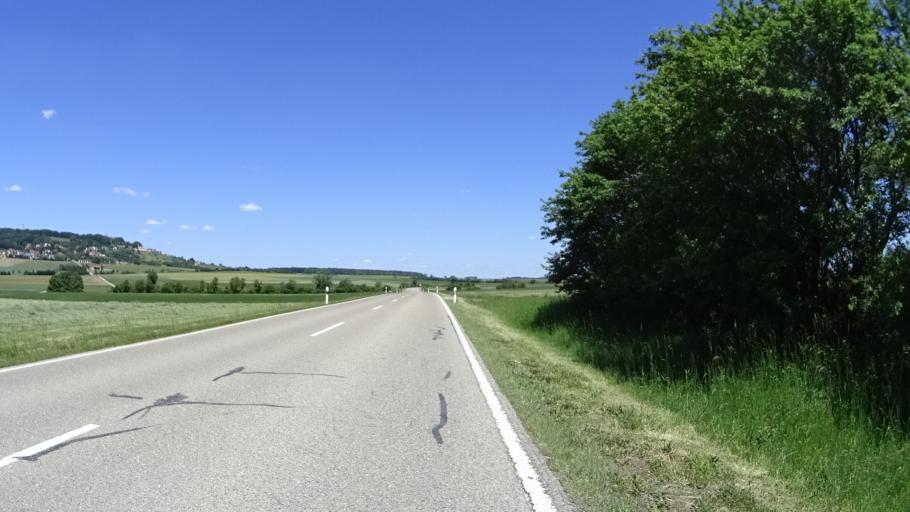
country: DE
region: Bavaria
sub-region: Regierungsbezirk Mittelfranken
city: Bergen
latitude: 49.0940
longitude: 11.1061
